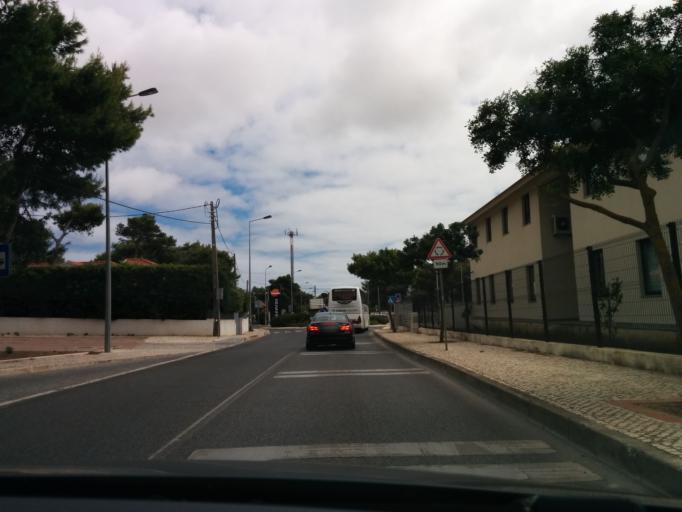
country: PT
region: Lisbon
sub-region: Cascais
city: Alcabideche
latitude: 38.7264
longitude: -9.4435
